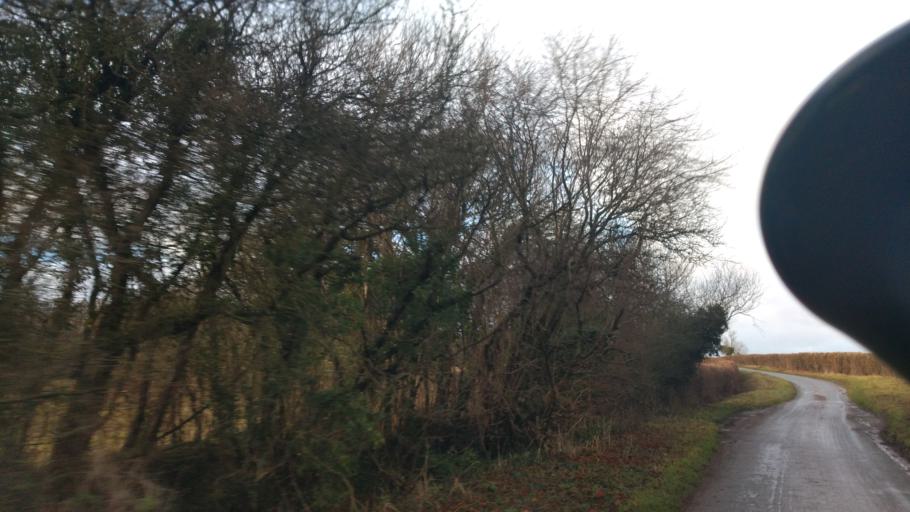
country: GB
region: England
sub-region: Wiltshire
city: Corsham
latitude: 51.4532
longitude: -2.1795
